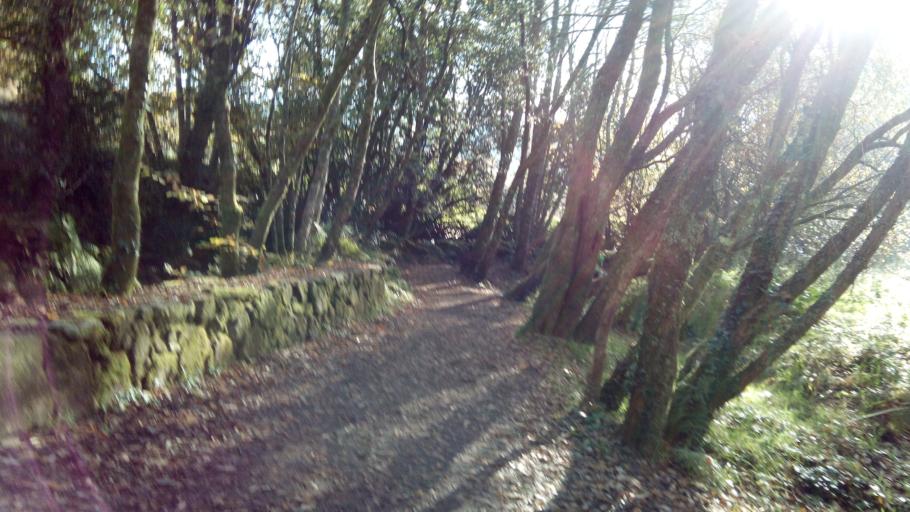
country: ES
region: Galicia
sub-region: Provincia de Pontevedra
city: Meis
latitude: 42.4839
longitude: -8.7429
